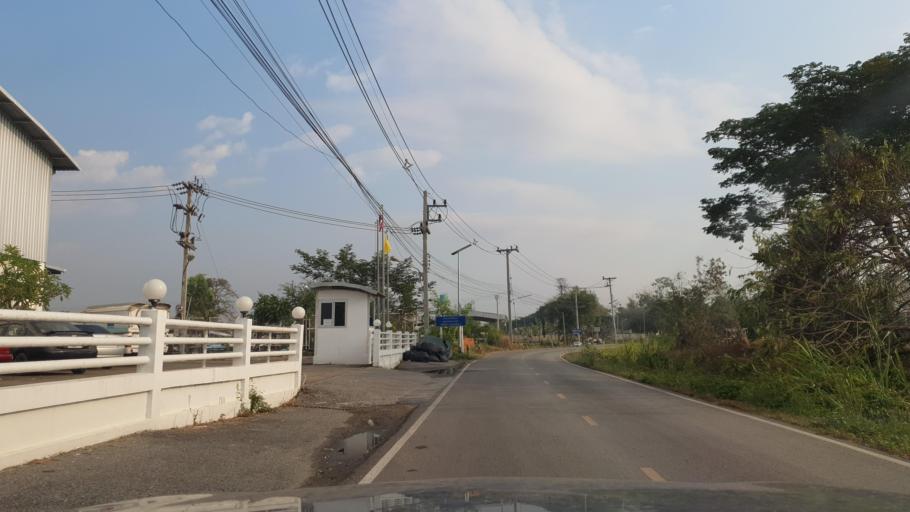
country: TH
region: Chiang Mai
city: San Kamphaeng
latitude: 18.7292
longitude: 99.1008
